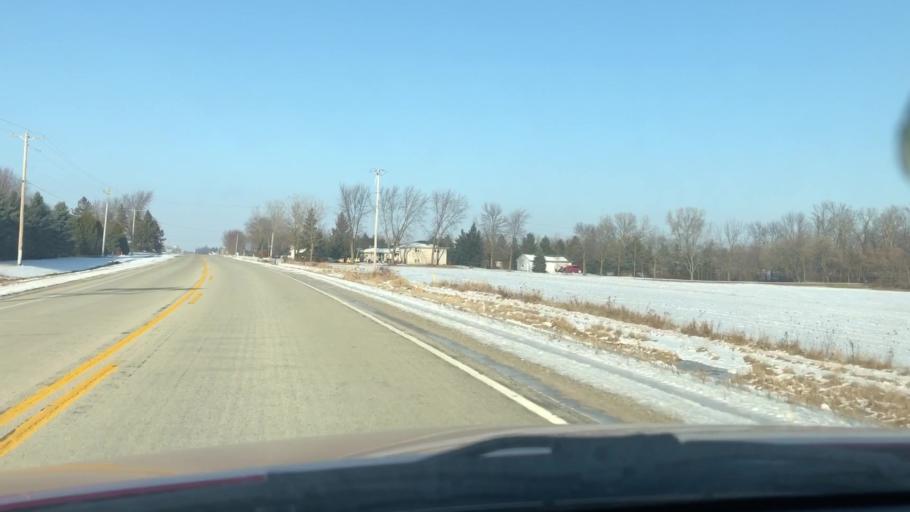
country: US
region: Wisconsin
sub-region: Outagamie County
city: Black Creek
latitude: 44.3973
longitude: -88.3745
